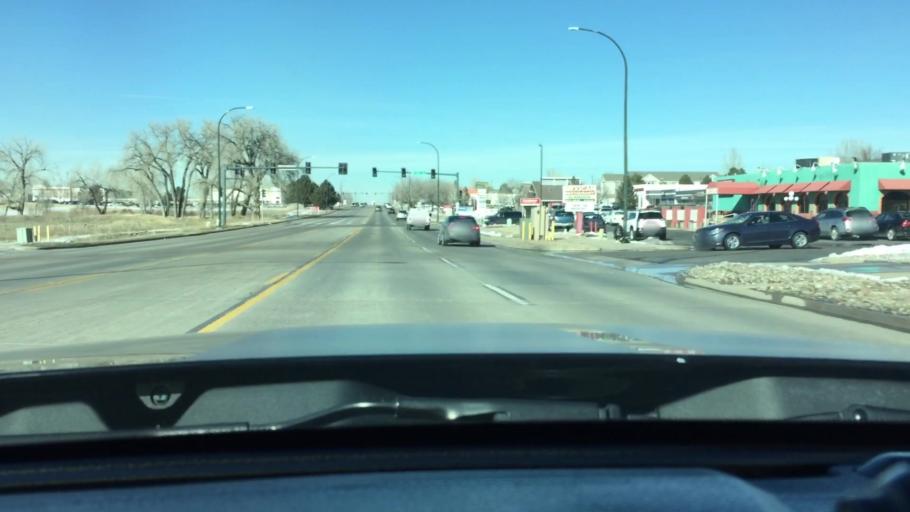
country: US
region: Colorado
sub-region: Adams County
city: Northglenn
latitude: 39.9024
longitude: -104.9967
